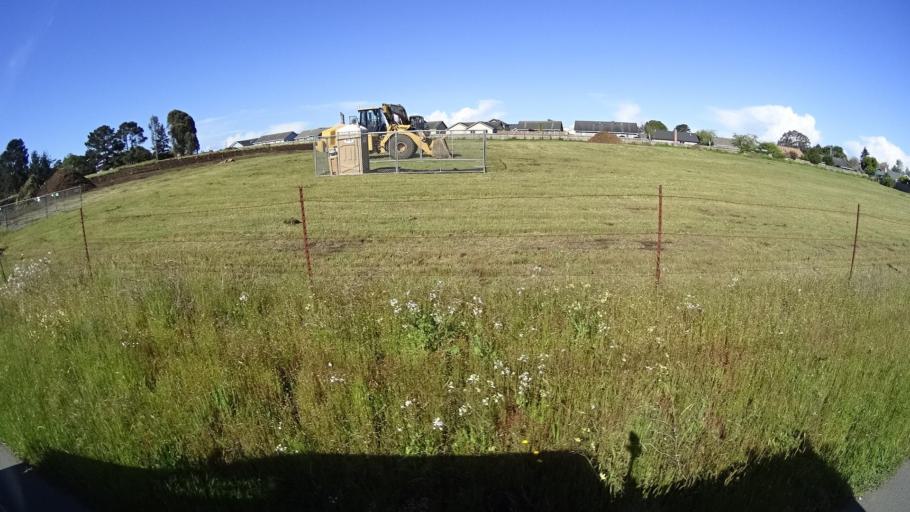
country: US
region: California
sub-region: Humboldt County
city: McKinleyville
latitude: 40.9364
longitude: -124.1073
